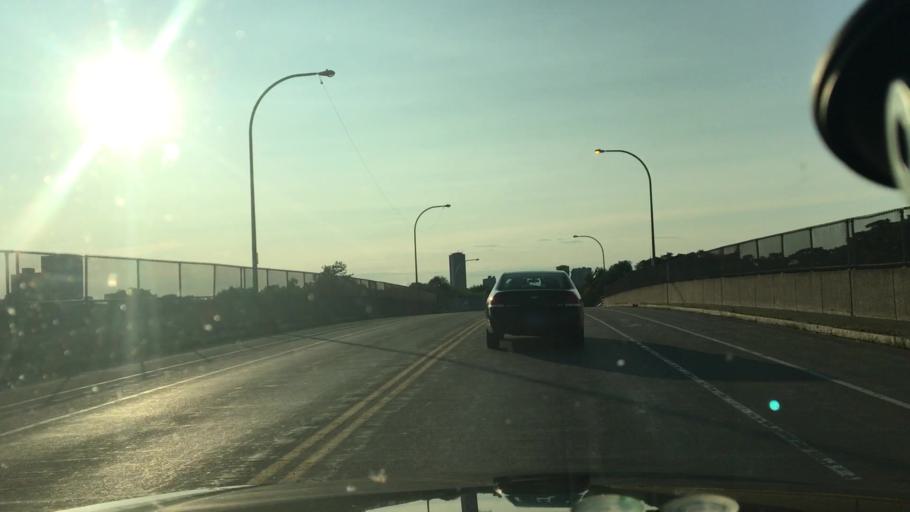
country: US
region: New York
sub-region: Erie County
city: Buffalo
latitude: 42.8647
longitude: -78.8454
